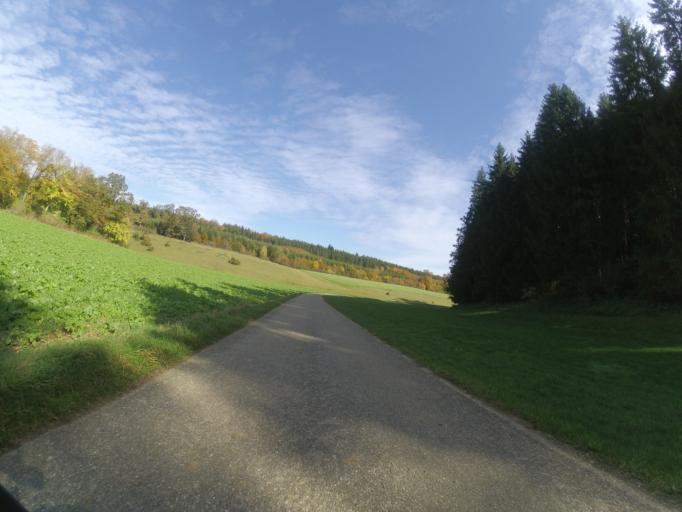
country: DE
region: Baden-Wuerttemberg
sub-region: Tuebingen Region
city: Weidenstetten
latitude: 48.5809
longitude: 9.9735
